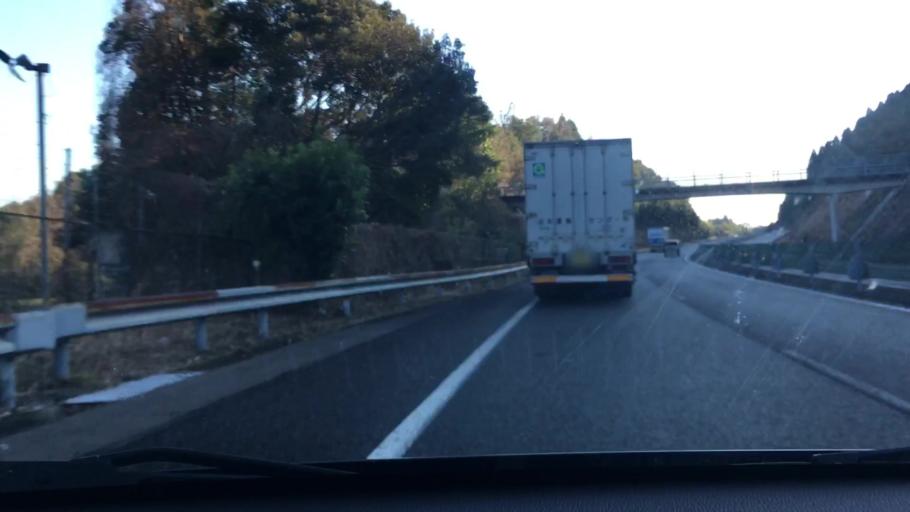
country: JP
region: Kagoshima
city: Kajiki
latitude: 31.8293
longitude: 130.6938
